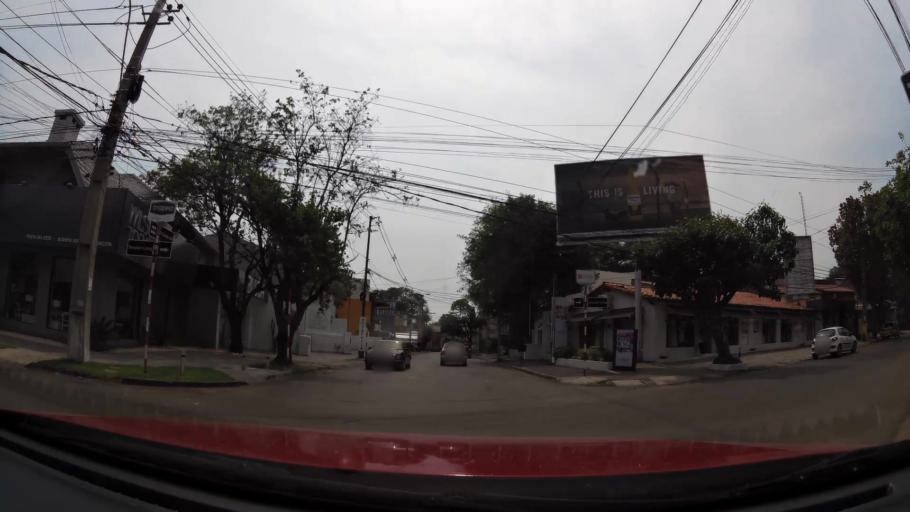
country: PY
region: Asuncion
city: Asuncion
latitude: -25.2882
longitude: -57.5769
